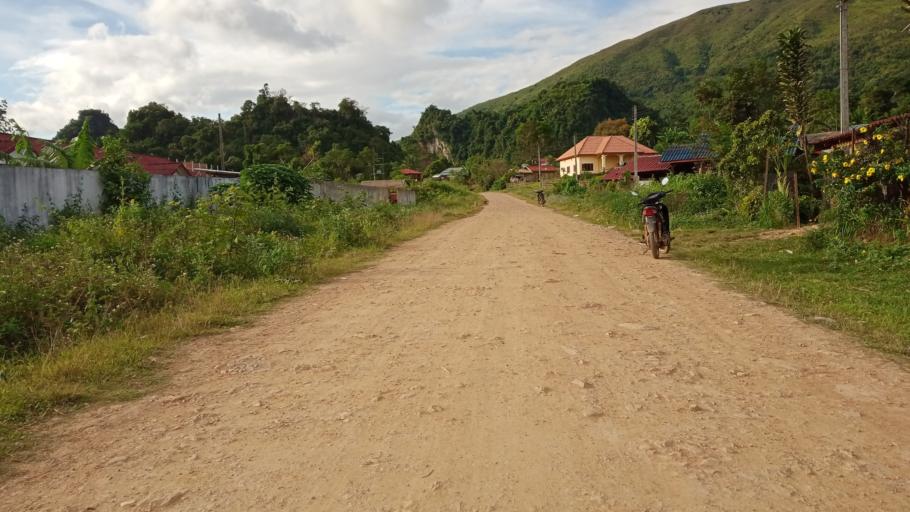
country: LA
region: Xiangkhoang
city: Phonsavan
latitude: 19.1084
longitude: 102.9265
